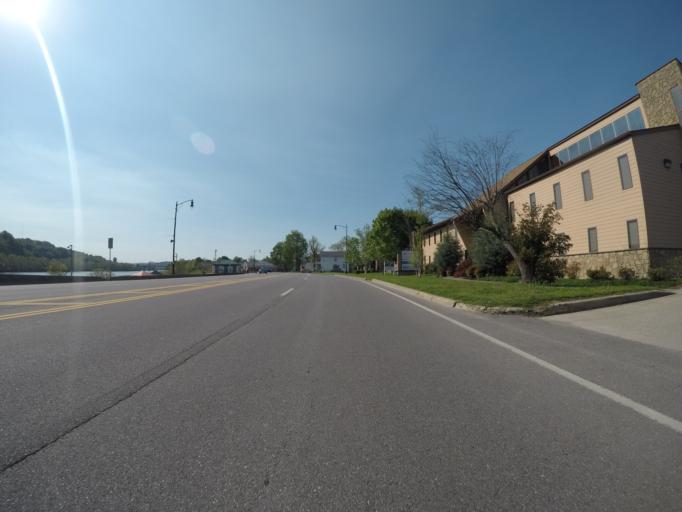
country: US
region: West Virginia
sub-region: Kanawha County
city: Charleston
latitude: 38.3570
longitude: -81.6471
